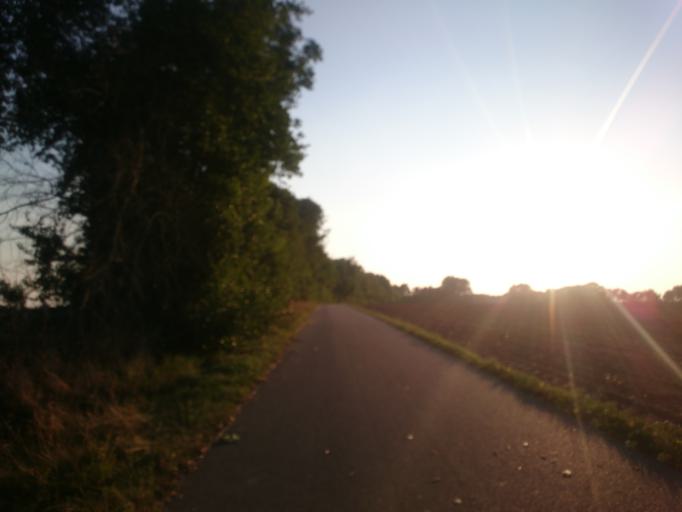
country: DE
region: Mecklenburg-Vorpommern
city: Barth
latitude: 54.3644
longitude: 12.7958
